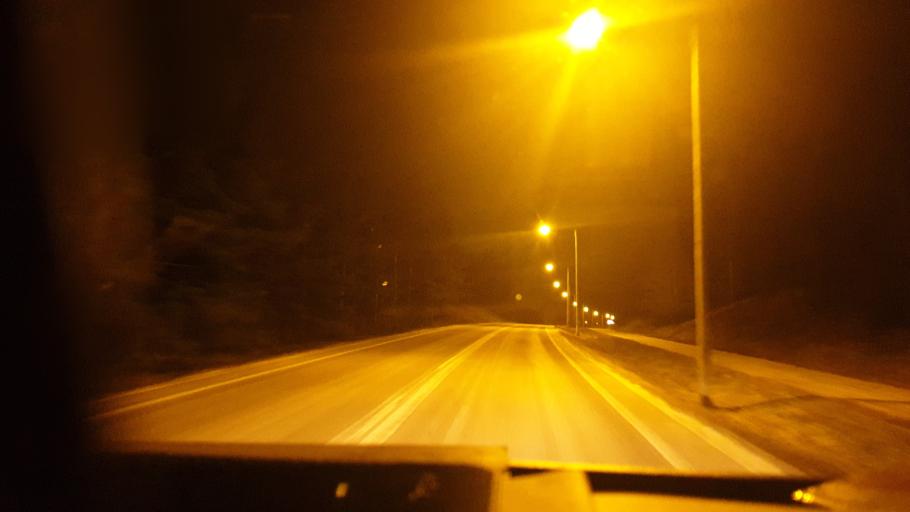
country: FI
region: Southern Ostrobothnia
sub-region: Kuusiokunnat
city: Alavus
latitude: 62.5969
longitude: 23.6515
